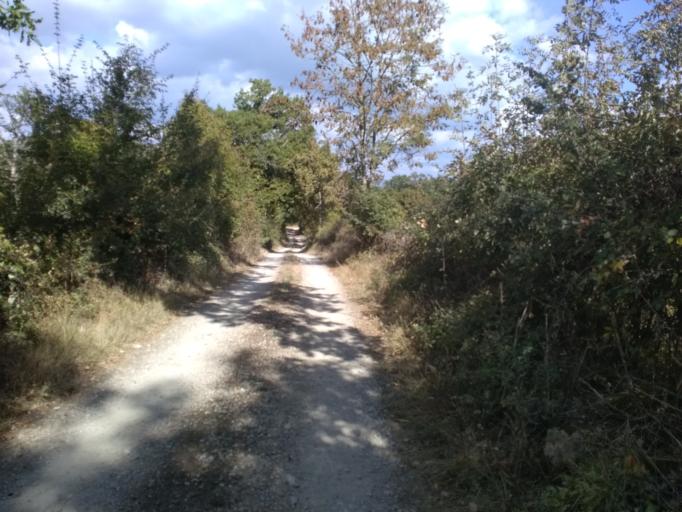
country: FR
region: Midi-Pyrenees
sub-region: Departement de l'Aveyron
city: Bozouls
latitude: 44.4667
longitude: 2.6742
